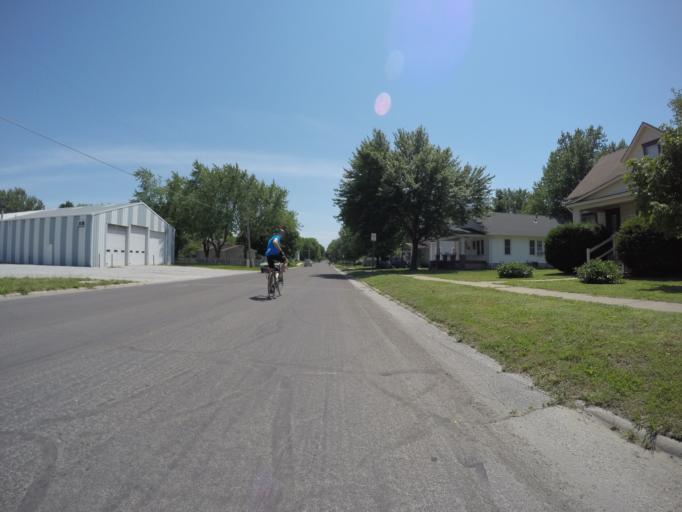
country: US
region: Kansas
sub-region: Nemaha County
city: Sabetha
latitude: 39.9079
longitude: -95.8072
